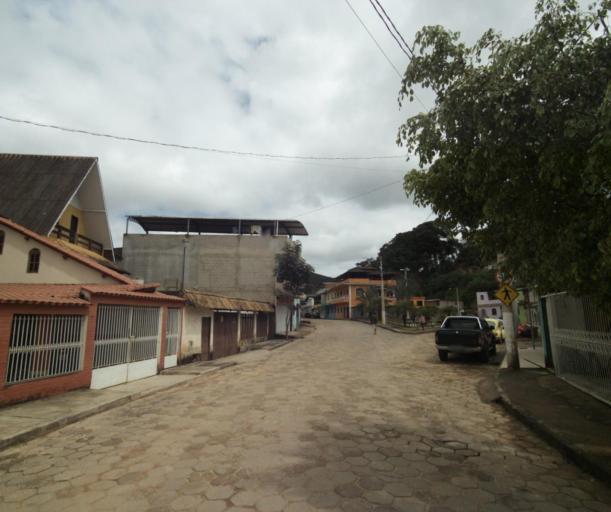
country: BR
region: Espirito Santo
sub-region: Irupi
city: Irupi
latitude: -20.3476
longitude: -41.6444
